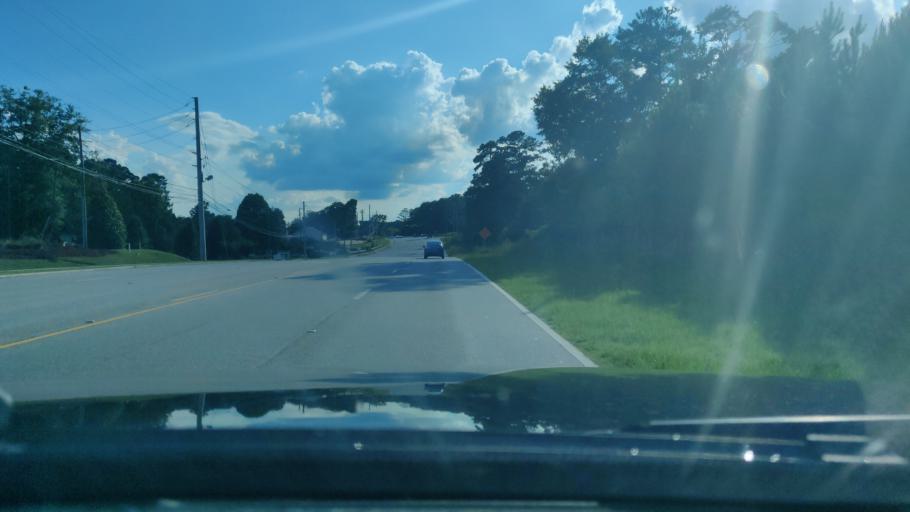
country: US
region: Alabama
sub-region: Lee County
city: Opelika
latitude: 32.6208
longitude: -85.4162
